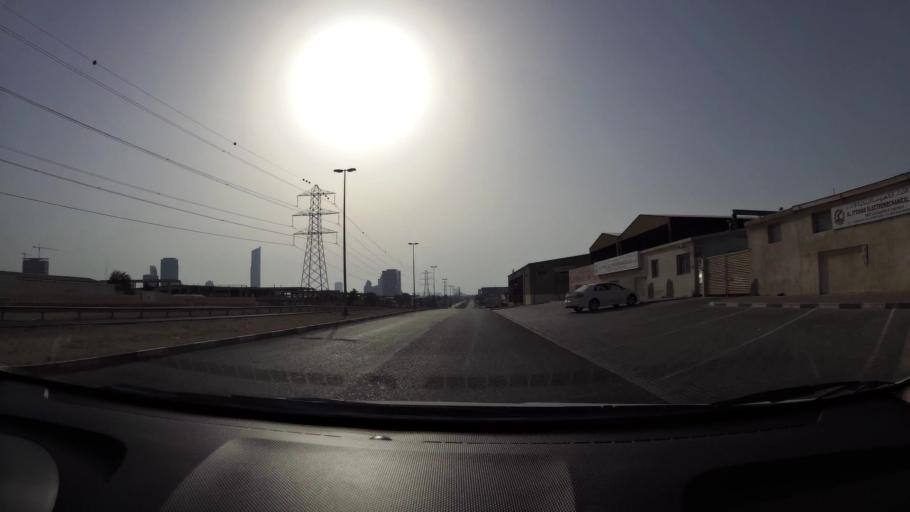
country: AE
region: Ash Shariqah
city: Sharjah
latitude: 25.2267
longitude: 55.3667
